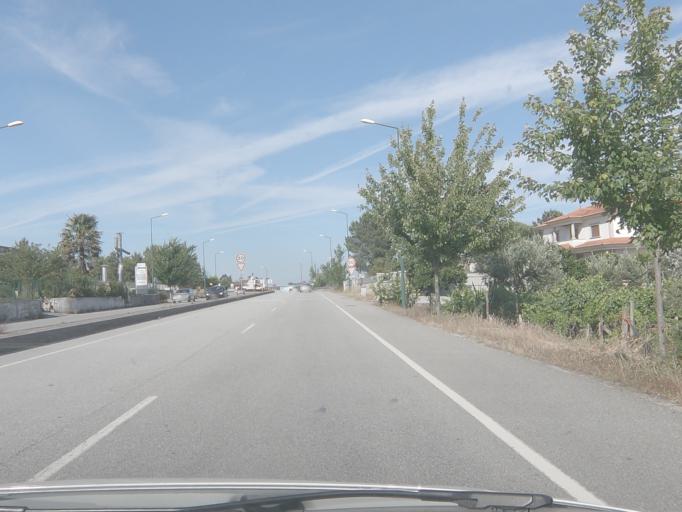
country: PT
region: Viseu
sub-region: Viseu
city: Viseu
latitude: 40.6211
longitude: -7.9478
